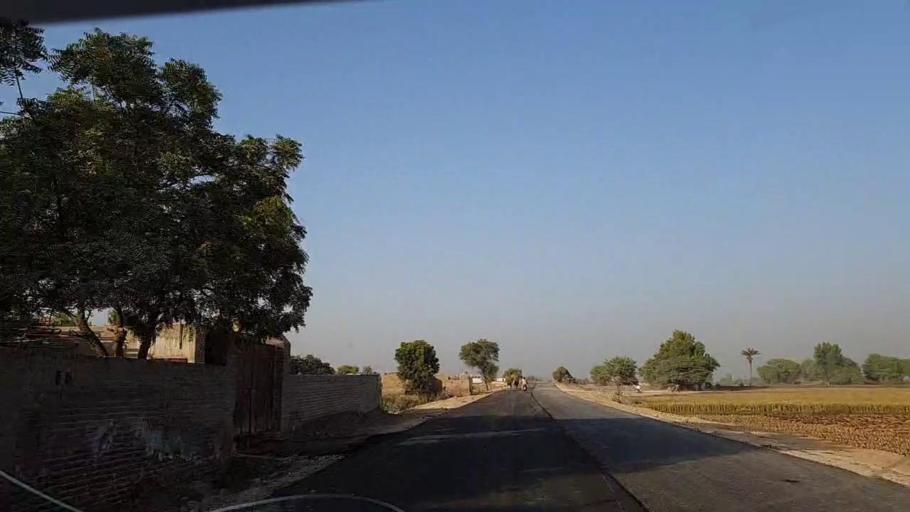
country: PK
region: Sindh
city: Rustam jo Goth
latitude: 27.9720
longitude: 68.8039
